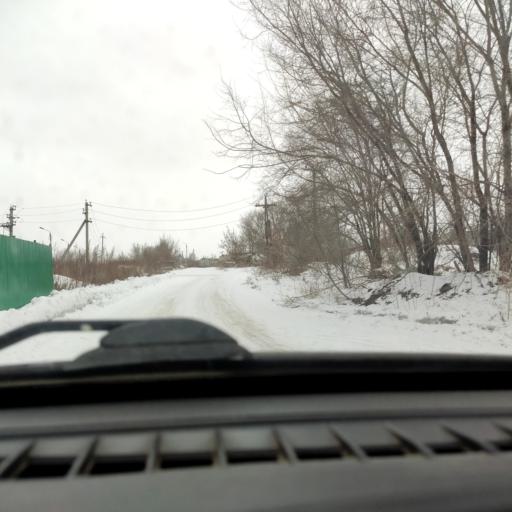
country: RU
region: Samara
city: Tol'yatti
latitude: 53.5682
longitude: 49.4707
